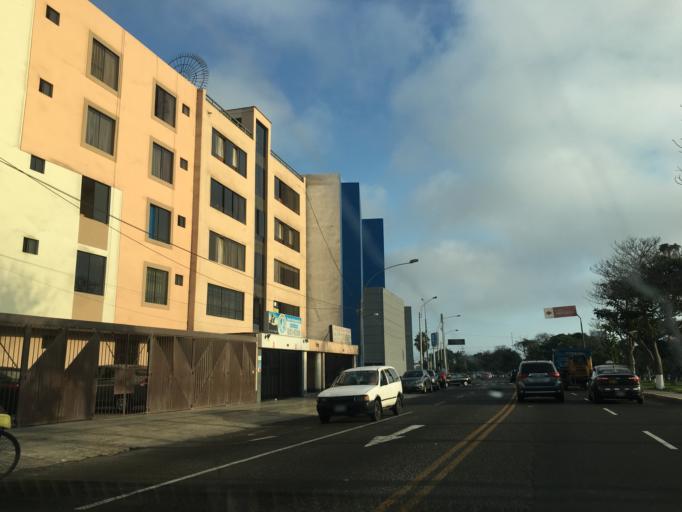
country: PE
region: Callao
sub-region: Callao
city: Callao
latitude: -12.0753
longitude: -77.0841
